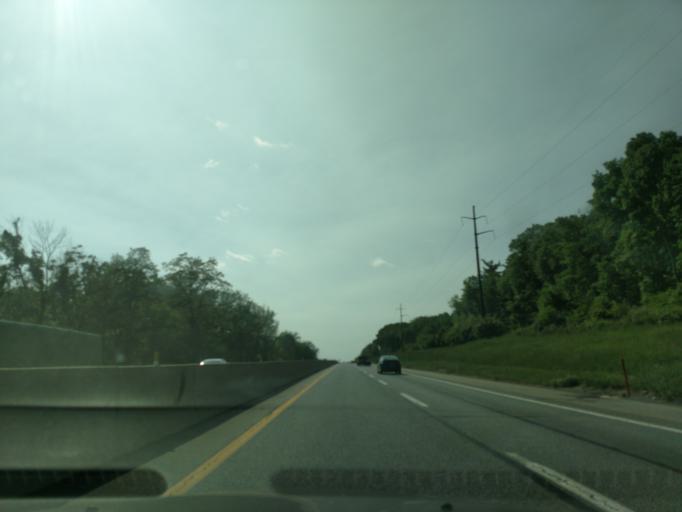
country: US
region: Pennsylvania
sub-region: Lancaster County
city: Reamstown
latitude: 40.2282
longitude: -76.1154
